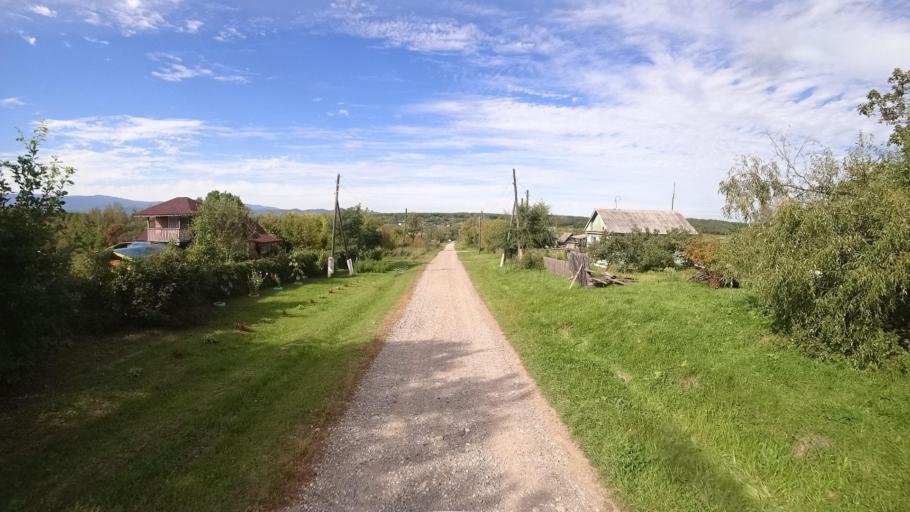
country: RU
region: Primorskiy
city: Dostoyevka
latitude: 44.3240
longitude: 133.4866
